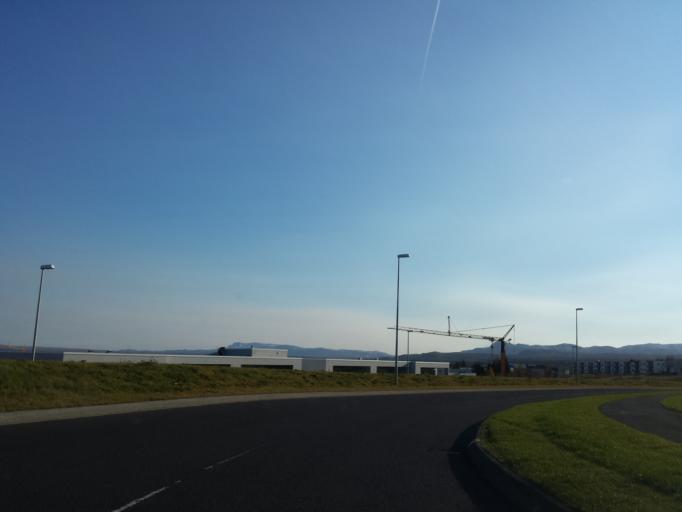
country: IS
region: Capital Region
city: Reykjavik
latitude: 64.0817
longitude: -21.8167
